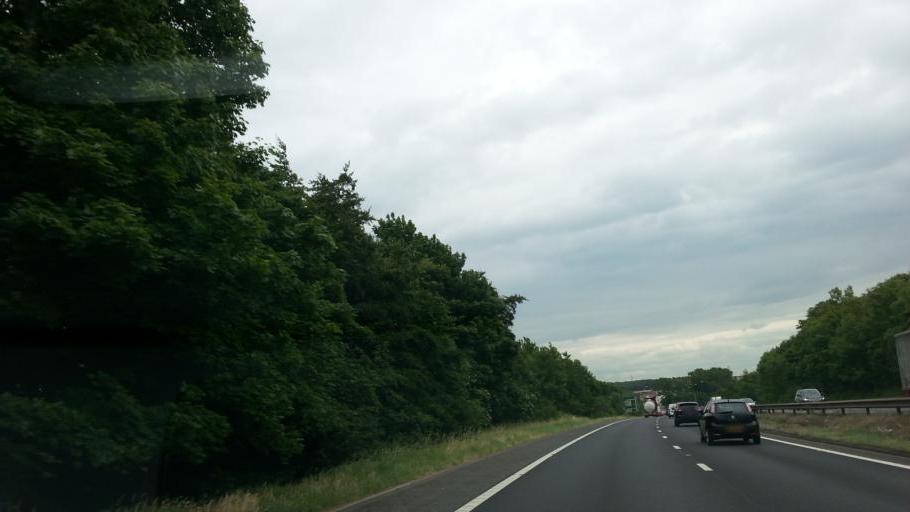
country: GB
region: England
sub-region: City and Borough of Wakefield
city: North Elmsall
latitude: 53.6319
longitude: -1.2415
